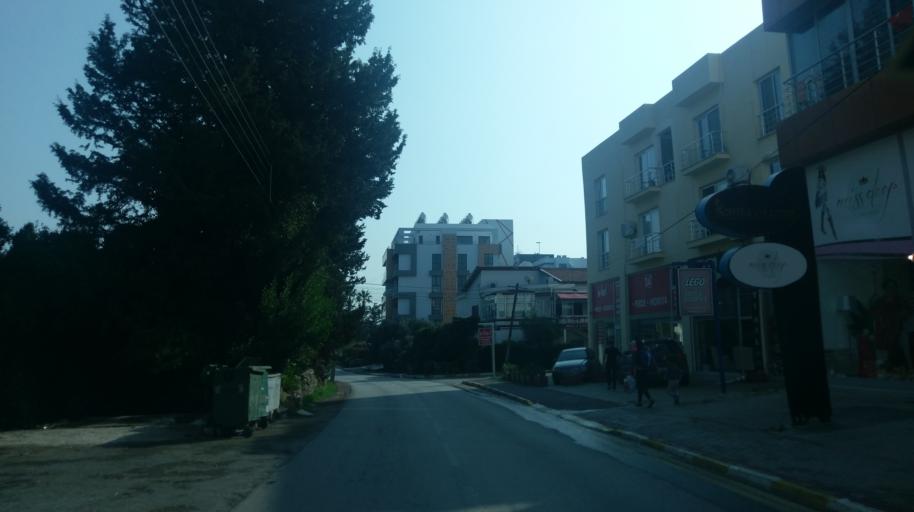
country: CY
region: Keryneia
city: Kyrenia
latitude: 35.3373
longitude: 33.3125
